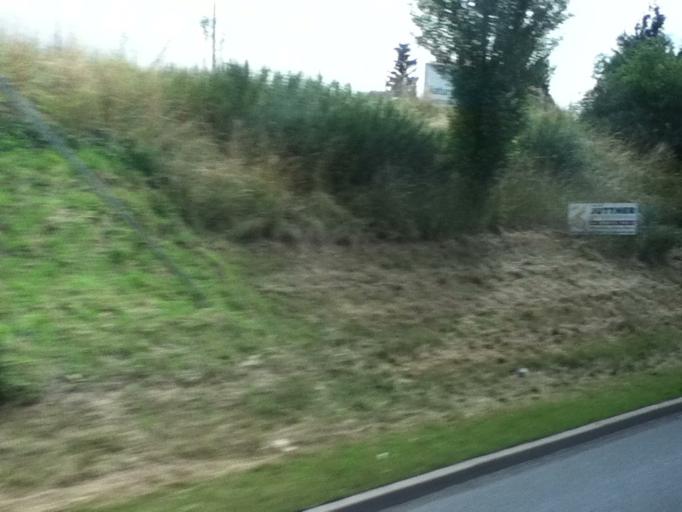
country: DE
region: Thuringia
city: Mellingen
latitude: 50.9435
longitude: 11.3990
